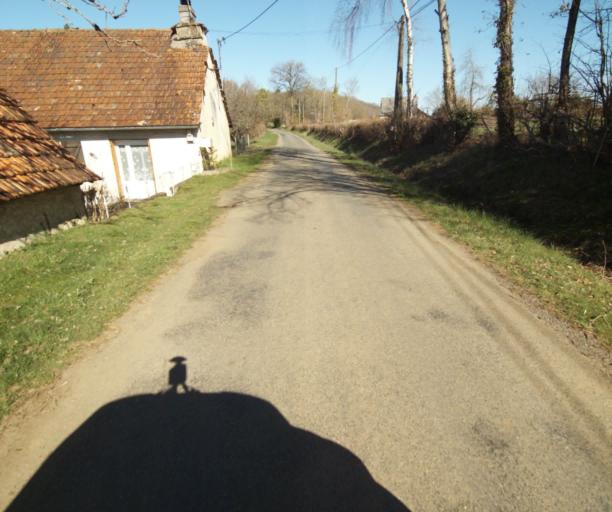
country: FR
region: Limousin
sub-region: Departement de la Correze
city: Seilhac
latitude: 45.3897
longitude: 1.7544
